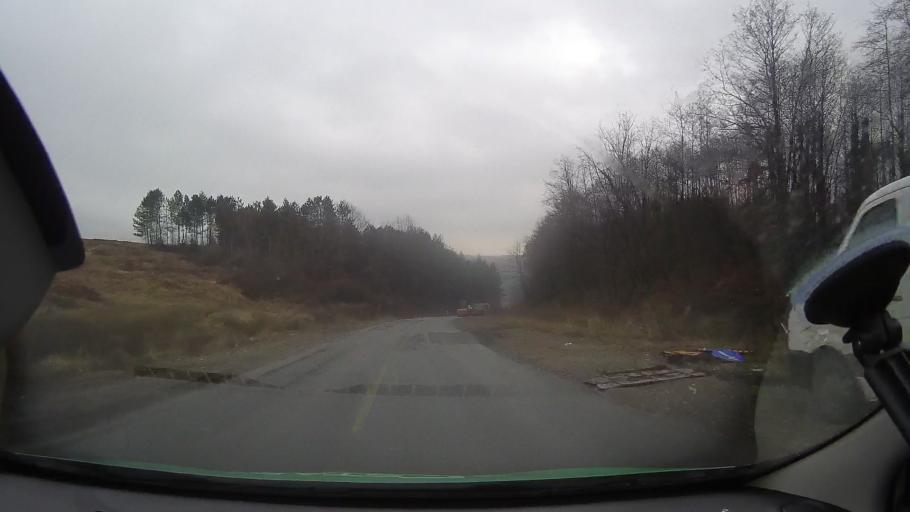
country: RO
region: Arad
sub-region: Comuna Halmagiu
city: Halmagiu
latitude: 46.2806
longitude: 22.5873
